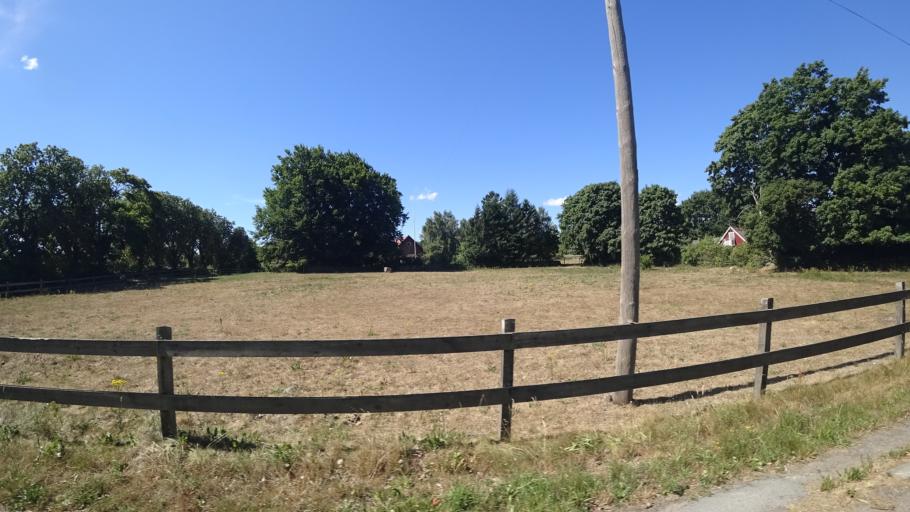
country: SE
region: Skane
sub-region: Kristianstads Kommun
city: Onnestad
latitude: 56.0440
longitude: 14.0333
